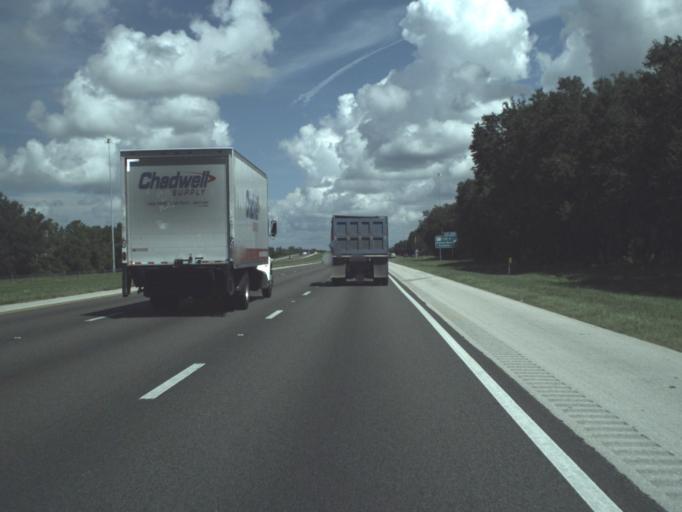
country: US
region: Florida
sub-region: Sarasota County
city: Lake Sarasota
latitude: 27.2619
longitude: -82.4489
